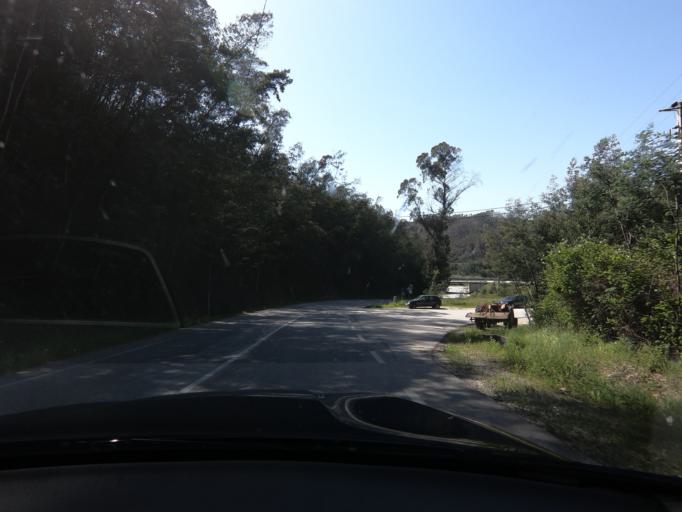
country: PT
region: Coimbra
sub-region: Penacova
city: Penacova
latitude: 40.2928
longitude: -8.2532
